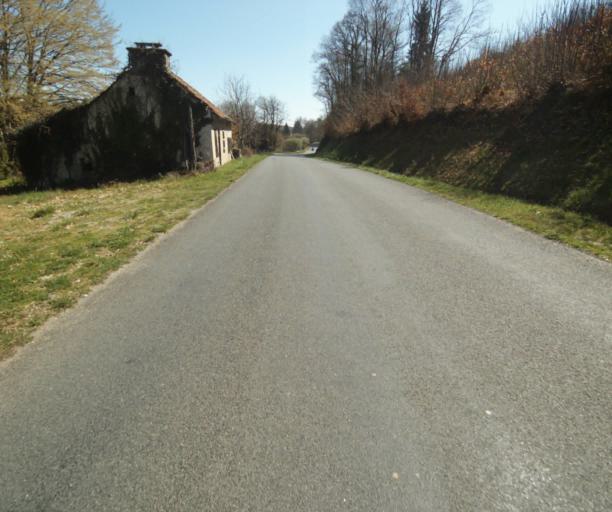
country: FR
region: Limousin
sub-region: Departement de la Correze
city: Saint-Mexant
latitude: 45.2778
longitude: 1.6620
